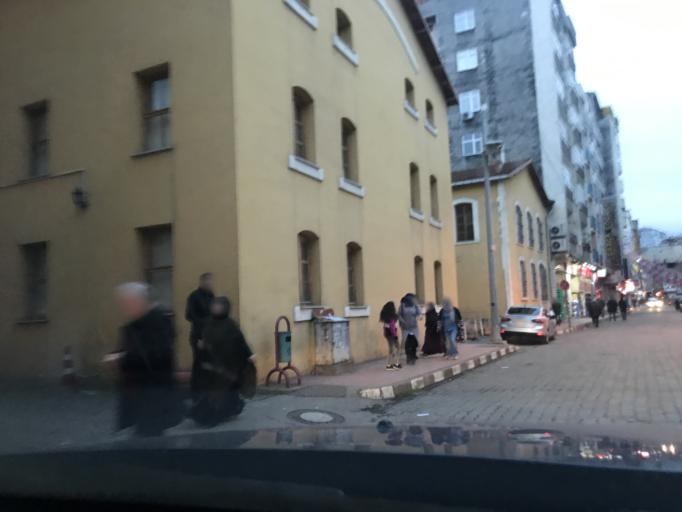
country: TR
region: Trabzon
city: Akcaabat
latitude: 41.0213
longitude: 39.5729
